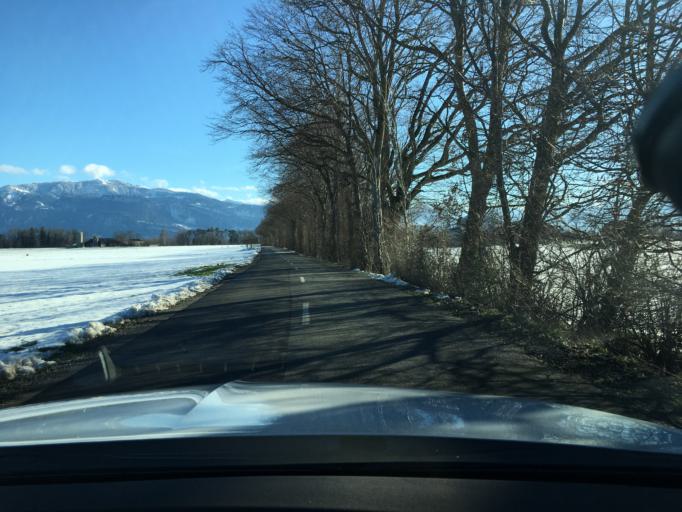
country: CH
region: Saint Gallen
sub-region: Wahlkreis Rheintal
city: Rebstein
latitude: 47.3853
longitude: 9.5802
